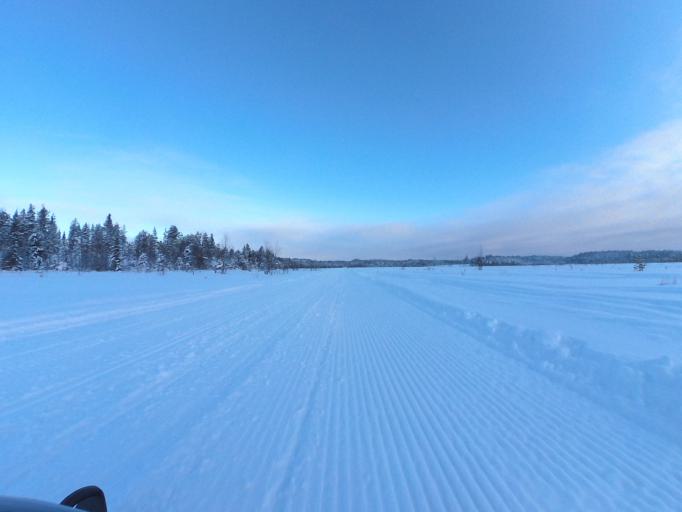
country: FI
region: Lapland
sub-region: Rovaniemi
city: Rovaniemi
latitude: 66.5143
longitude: 25.9899
